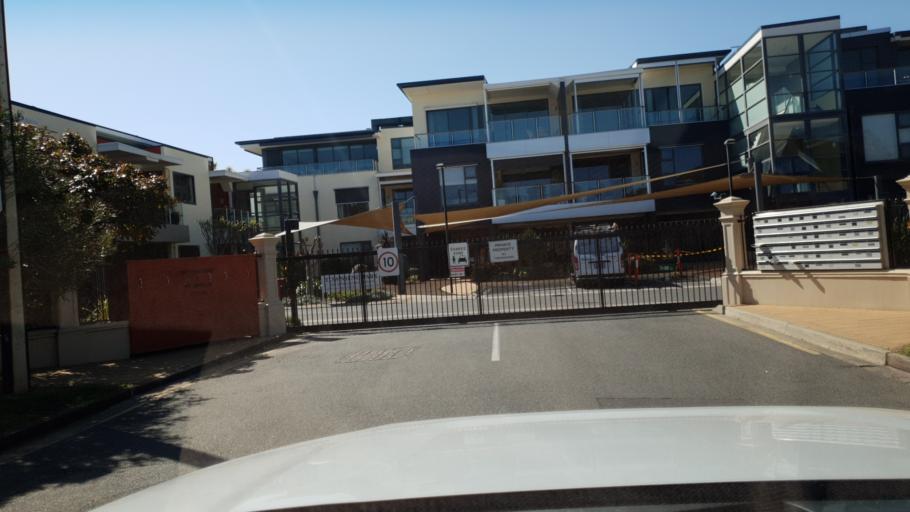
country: AU
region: South Australia
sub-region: Adelaide
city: Brighton
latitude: -35.0127
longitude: 138.5147
